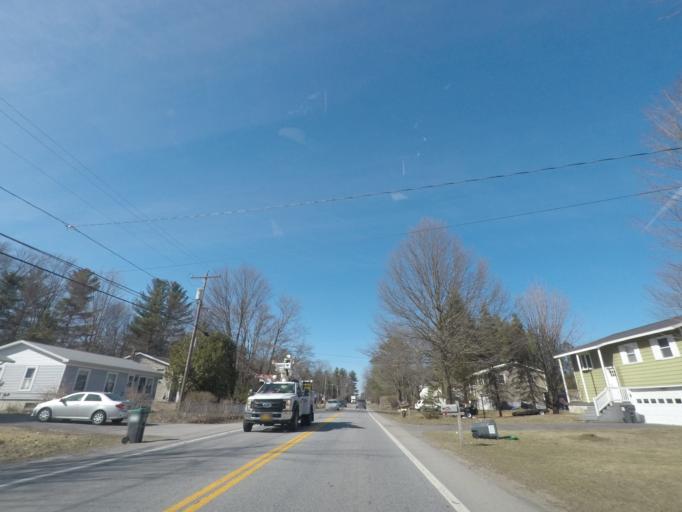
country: US
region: New York
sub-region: Saratoga County
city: Milton
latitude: 43.0349
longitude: -73.8491
